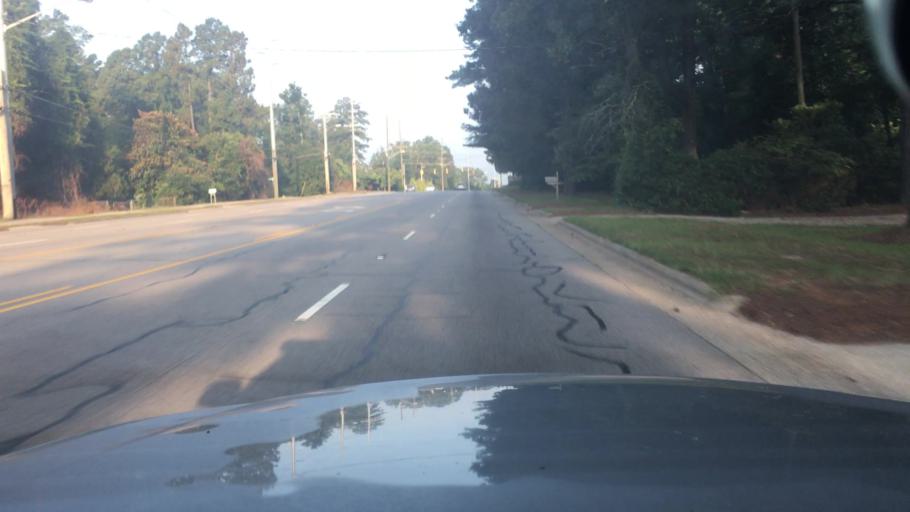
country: US
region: North Carolina
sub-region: Cumberland County
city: Fayetteville
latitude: 35.1046
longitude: -78.8839
